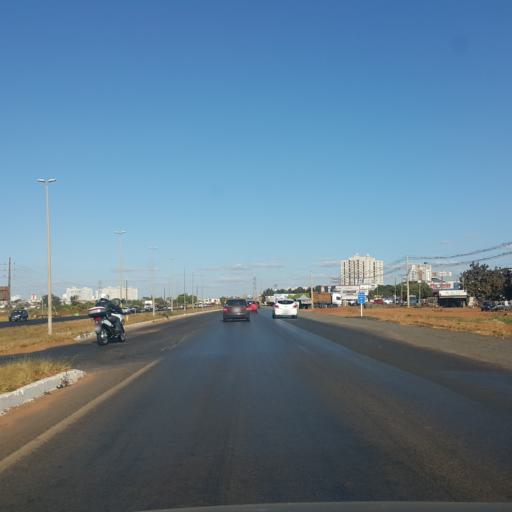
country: BR
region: Federal District
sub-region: Brasilia
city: Brasilia
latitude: -15.7986
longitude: -48.0892
